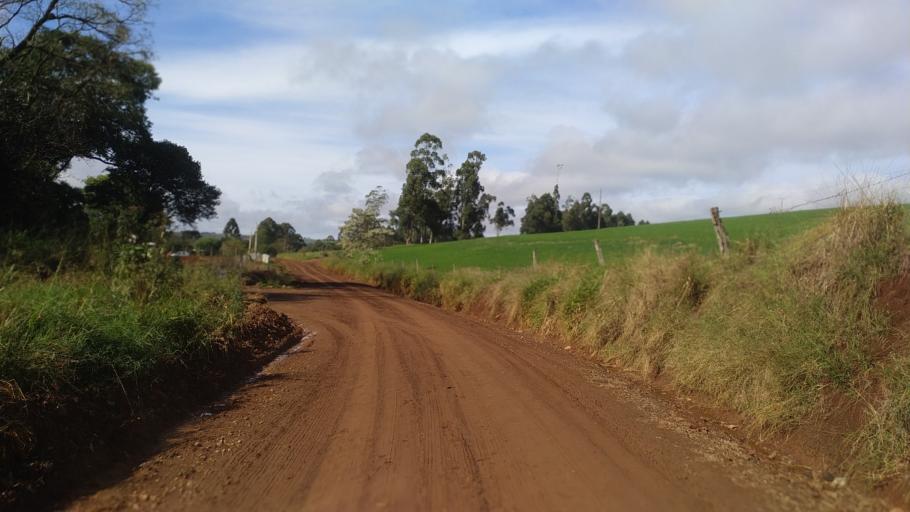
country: BR
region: Santa Catarina
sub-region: Chapeco
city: Chapeco
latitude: -27.1615
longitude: -52.6050
